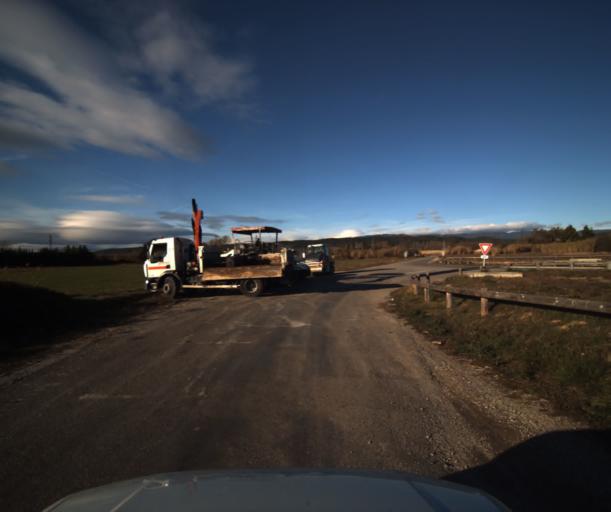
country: FR
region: Provence-Alpes-Cote d'Azur
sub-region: Departement du Vaucluse
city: Pertuis
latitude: 43.6876
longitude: 5.4824
